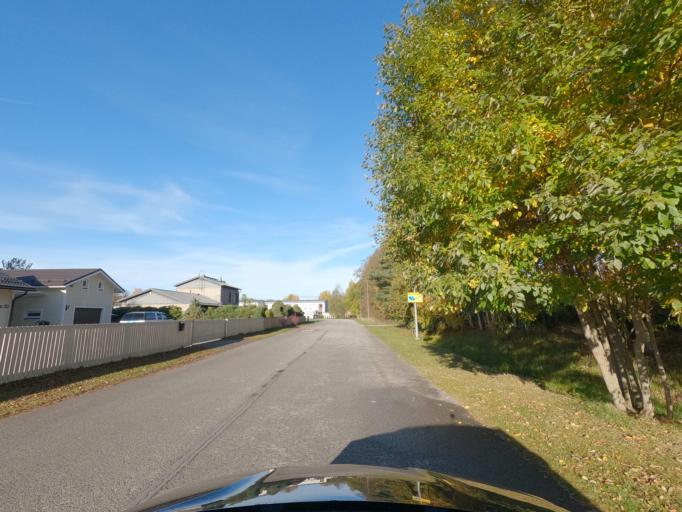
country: EE
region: Harju
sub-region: Kiili vald
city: Kiili
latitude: 59.3087
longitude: 24.7516
